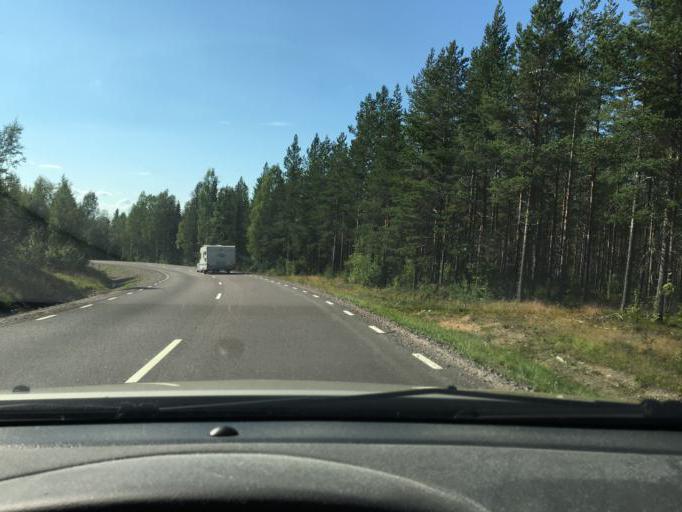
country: SE
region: Norrbotten
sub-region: Lulea Kommun
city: Ranea
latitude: 66.0523
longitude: 22.2186
